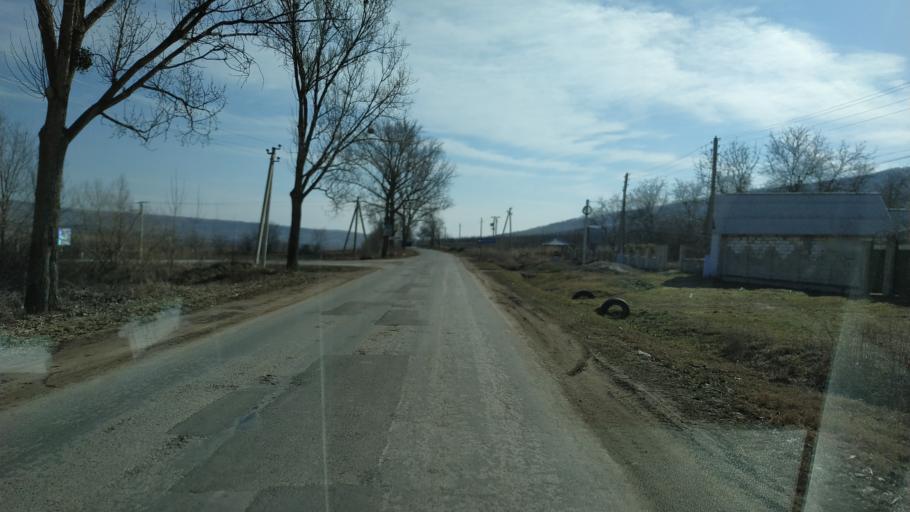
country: MD
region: Nisporeni
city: Nisporeni
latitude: 47.1473
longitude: 28.1091
